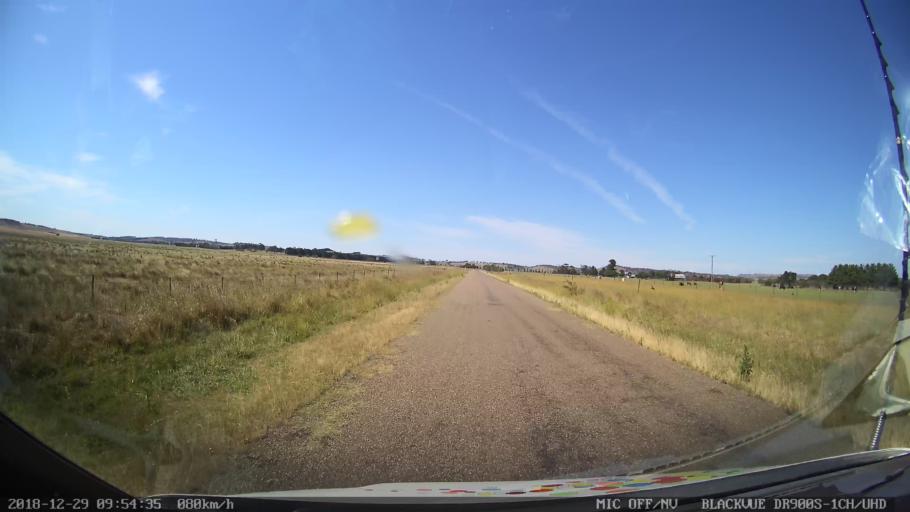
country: AU
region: New South Wales
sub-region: Goulburn Mulwaree
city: Goulburn
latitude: -34.7649
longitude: 149.4667
